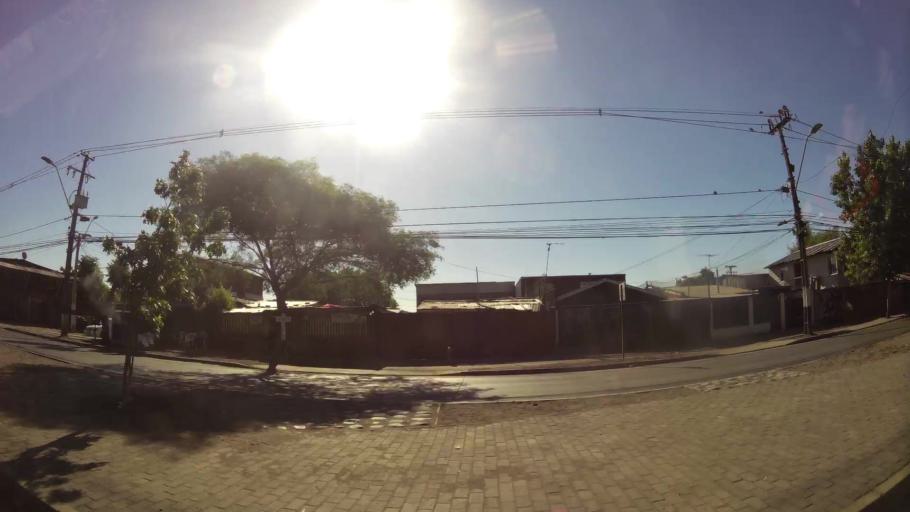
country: CL
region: Santiago Metropolitan
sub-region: Provincia de Maipo
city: San Bernardo
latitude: -33.5921
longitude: -70.6793
